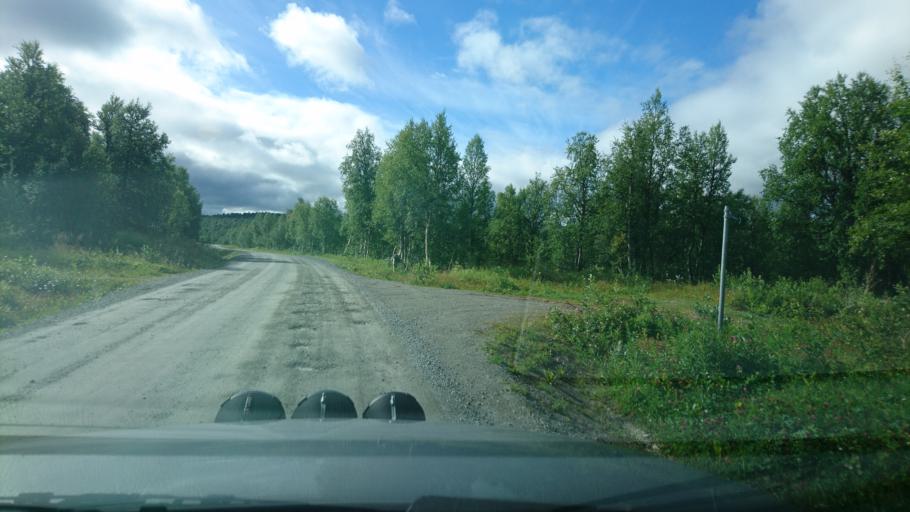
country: NO
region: Nordland
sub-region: Hattfjelldal
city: Hattfjelldal
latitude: 65.7094
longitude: 15.0984
